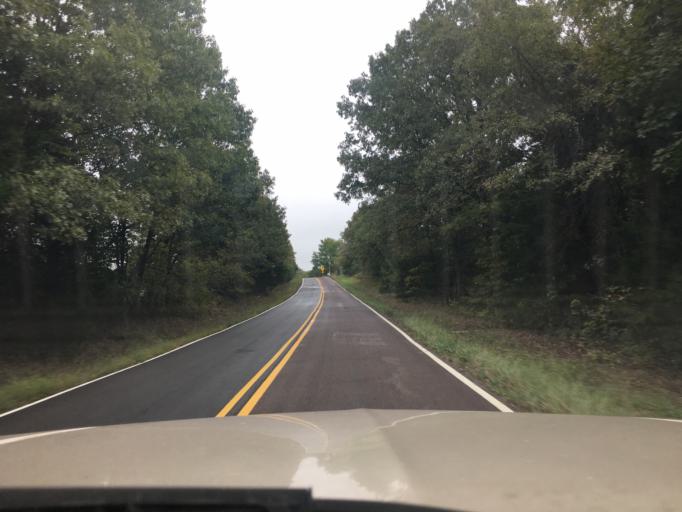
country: US
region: Missouri
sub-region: Crawford County
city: Cuba
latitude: 38.1914
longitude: -91.4760
